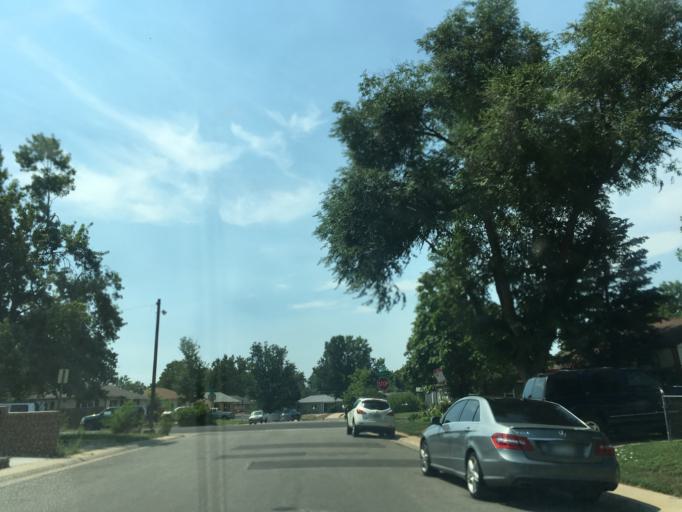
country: US
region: Colorado
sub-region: Jefferson County
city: Lakewood
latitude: 39.6937
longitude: -105.0473
